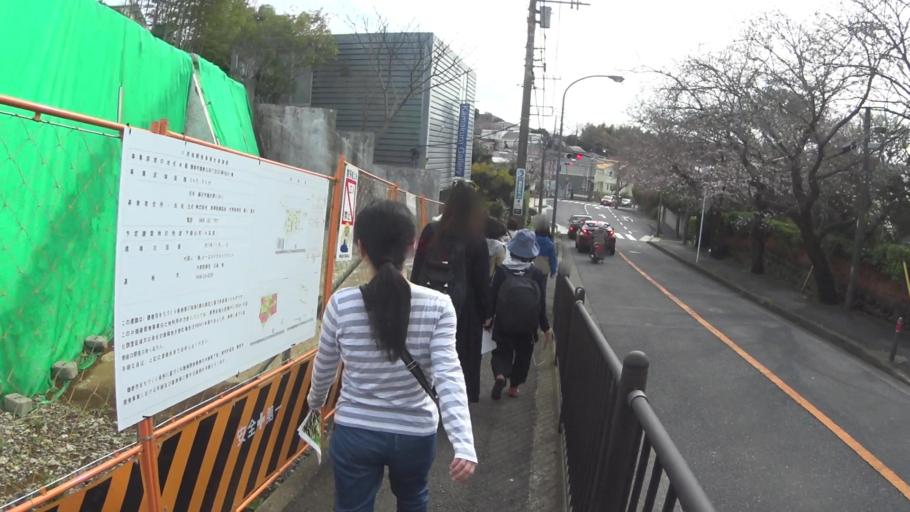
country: JP
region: Kanagawa
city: Kamakura
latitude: 35.3234
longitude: 139.5134
